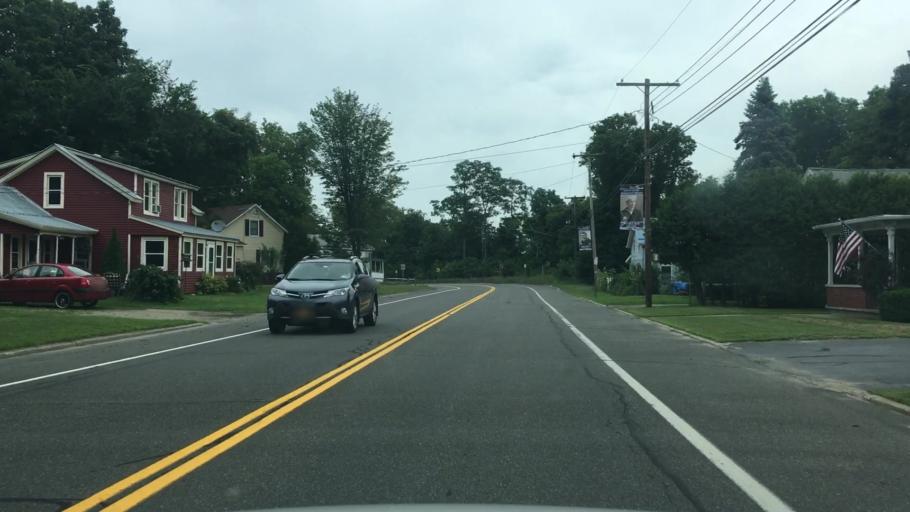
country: US
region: New York
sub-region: Essex County
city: Keeseville
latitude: 44.5023
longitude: -73.4874
